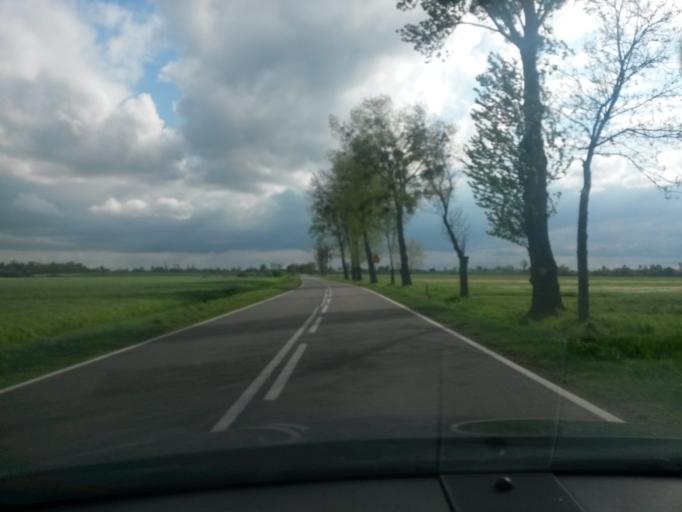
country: PL
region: Masovian Voivodeship
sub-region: Powiat sierpecki
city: Zawidz
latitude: 52.8579
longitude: 19.8470
